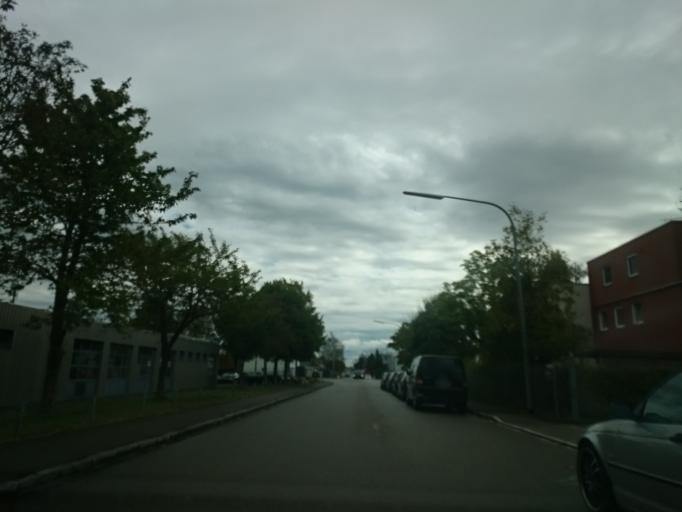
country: DE
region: Bavaria
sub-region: Swabia
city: Oberottmarshausen
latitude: 48.2533
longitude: 10.8708
